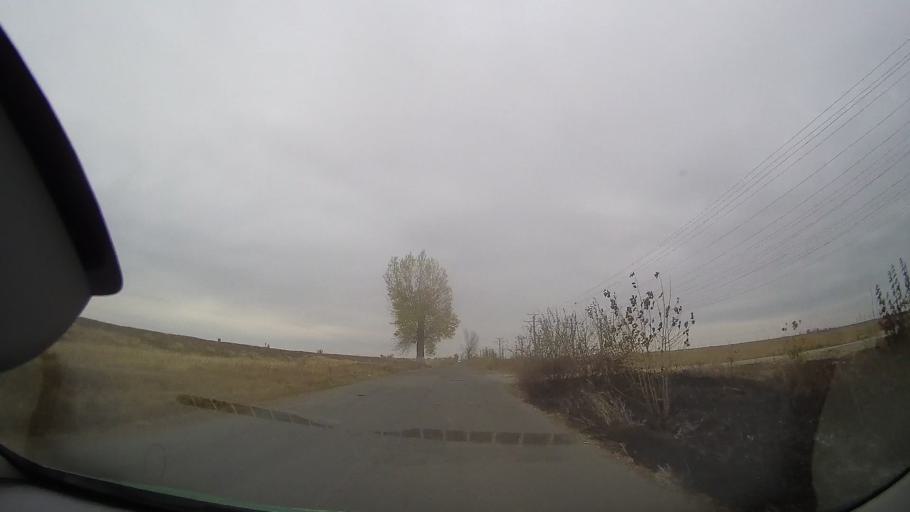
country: RO
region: Braila
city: Dudesti
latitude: 44.9129
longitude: 27.4303
